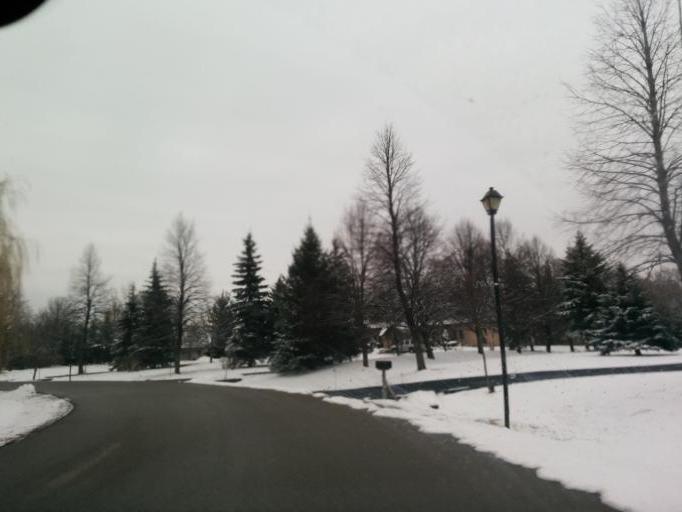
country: CA
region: Ontario
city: Brampton
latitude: 43.7607
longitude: -79.6547
